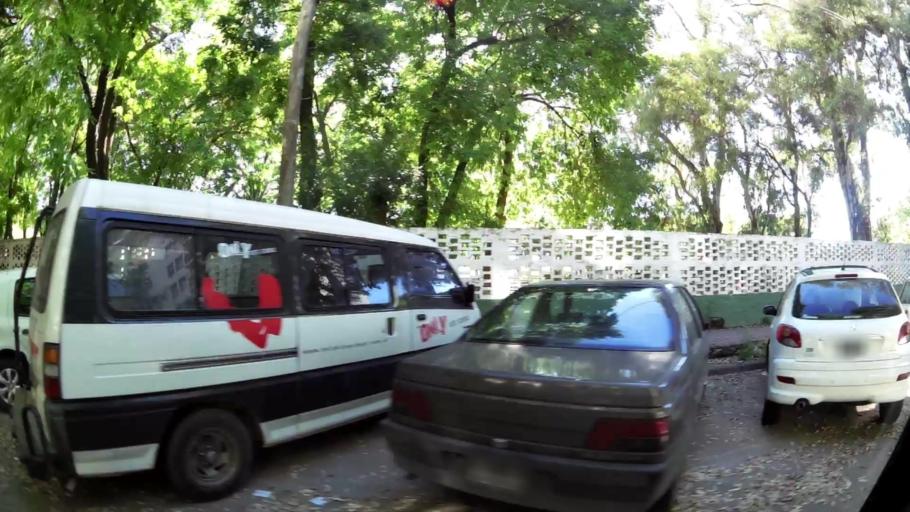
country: AR
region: Buenos Aires
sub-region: Partido de Vicente Lopez
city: Olivos
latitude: -34.5231
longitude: -58.4715
